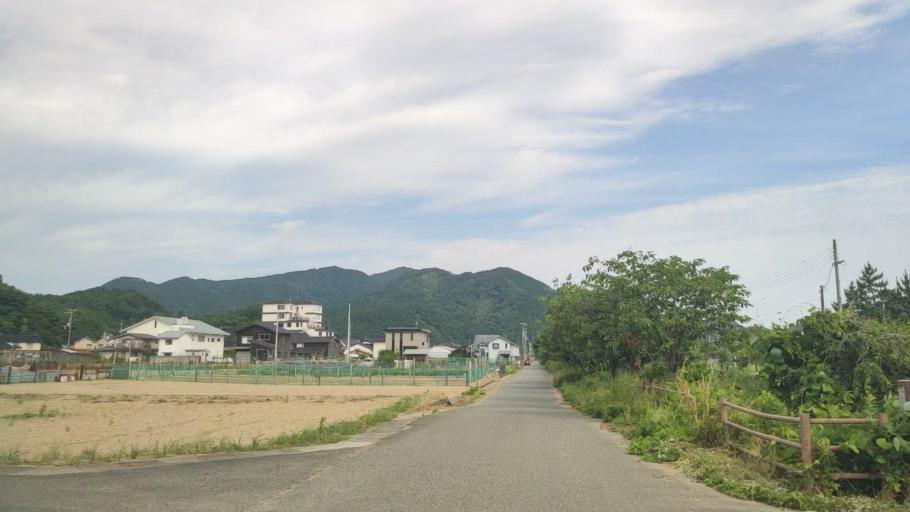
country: JP
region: Hyogo
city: Toyooka
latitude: 35.6404
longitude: 134.8383
